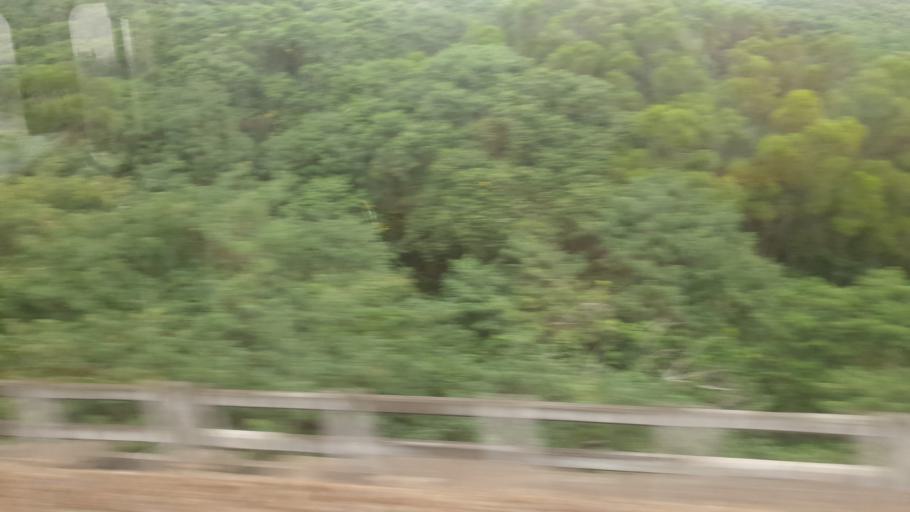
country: TW
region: Taiwan
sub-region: Hsinchu
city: Zhubei
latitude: 24.8534
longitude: 121.0106
